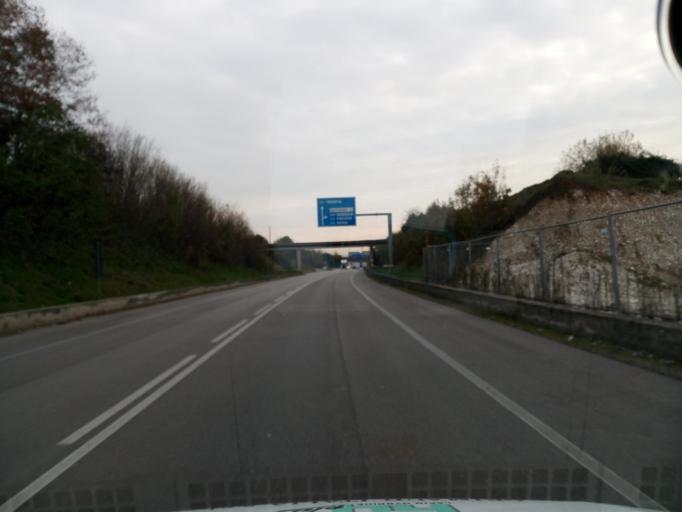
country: IT
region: Veneto
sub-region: Provincia di Vicenza
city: San Zeno-San Giuseppe
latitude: 45.7364
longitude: 11.7546
